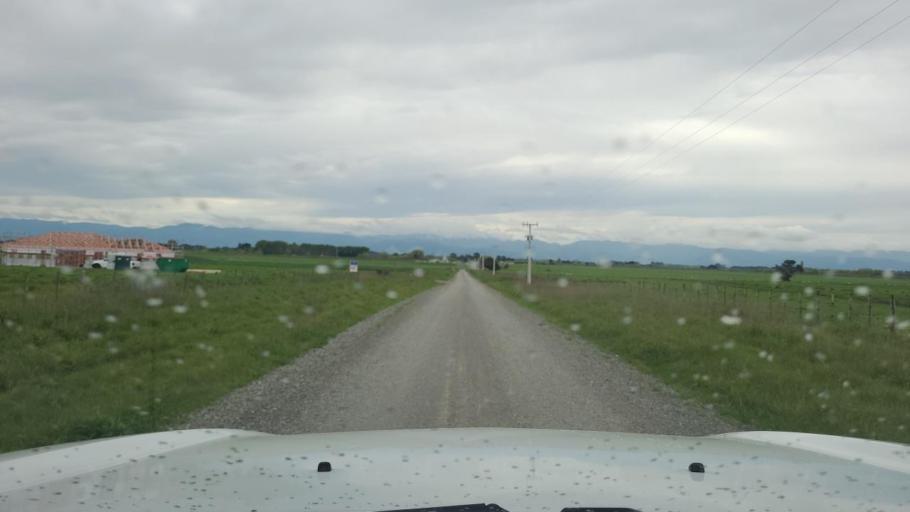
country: NZ
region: Wellington
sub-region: South Wairarapa District
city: Waipawa
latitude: -41.2618
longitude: 175.3777
